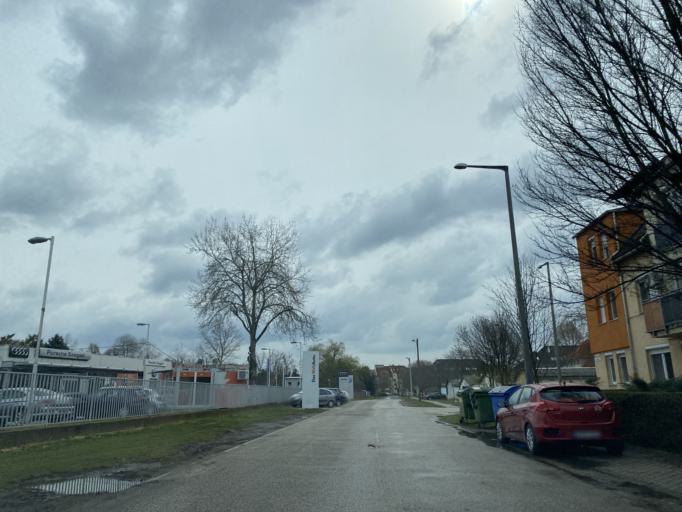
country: HU
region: Csongrad
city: Szeged
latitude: 46.2676
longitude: 20.1445
